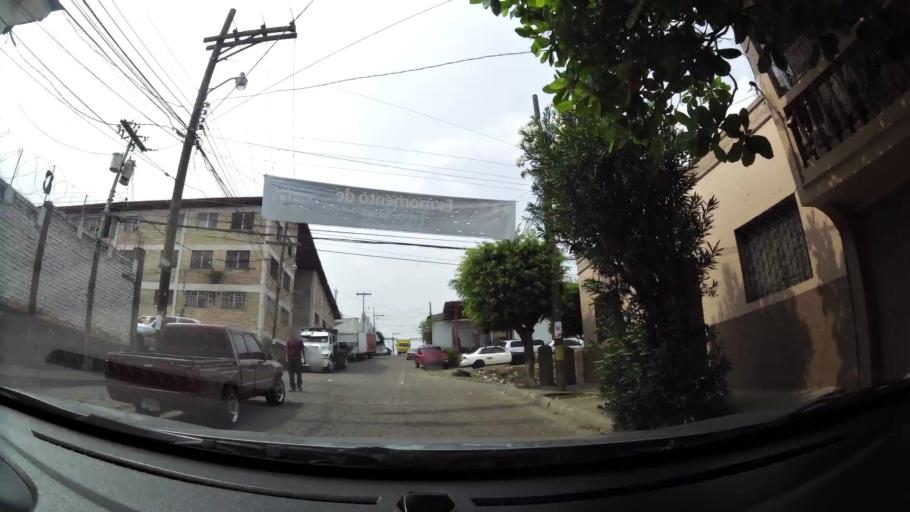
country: HN
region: Francisco Morazan
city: Tegucigalpa
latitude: 14.0920
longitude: -87.2131
